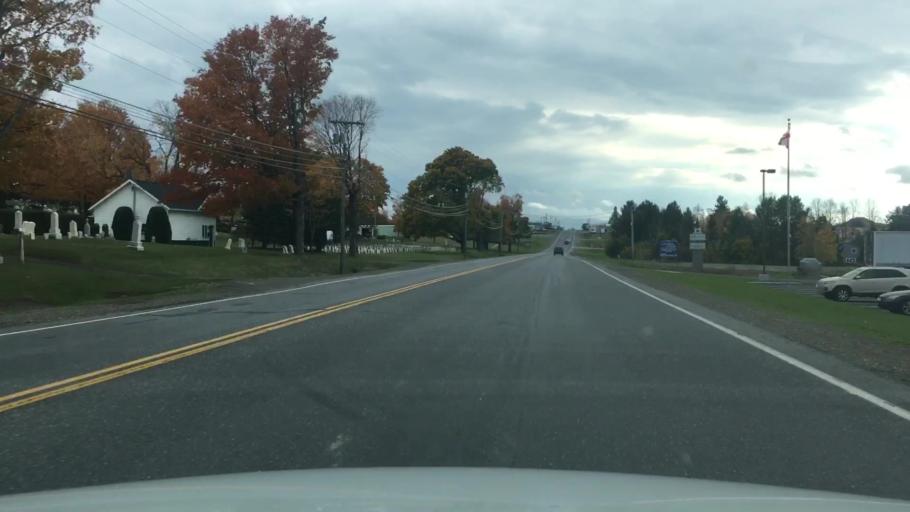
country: US
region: Maine
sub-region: Aroostook County
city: Presque Isle
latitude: 46.6649
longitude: -68.0102
